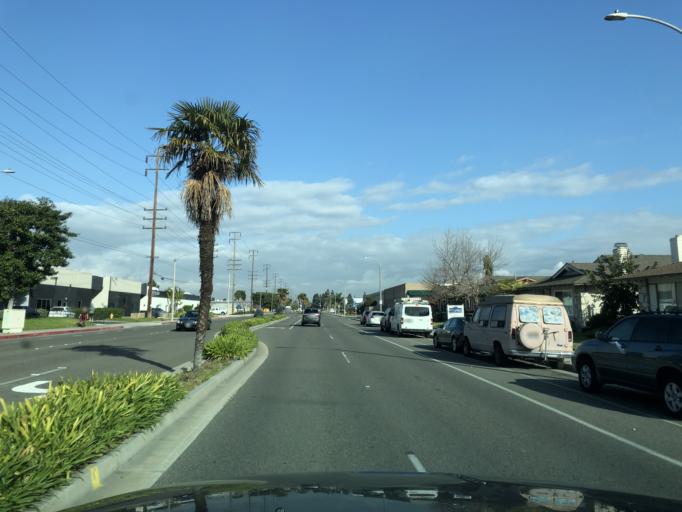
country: US
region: California
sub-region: Orange County
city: Westminster
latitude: 33.7328
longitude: -118.0326
